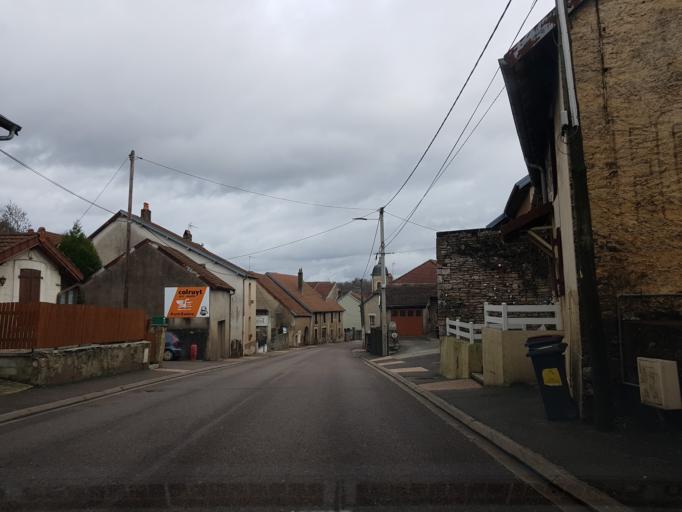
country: FR
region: Franche-Comte
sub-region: Departement de la Haute-Saone
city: Port-sur-Saone
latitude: 47.6916
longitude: 6.0343
